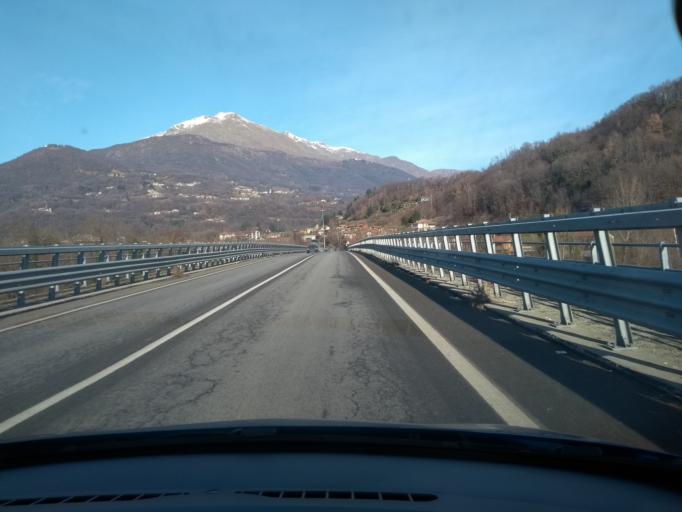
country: IT
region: Piedmont
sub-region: Provincia di Torino
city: Cuorgne
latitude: 45.3929
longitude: 7.6604
